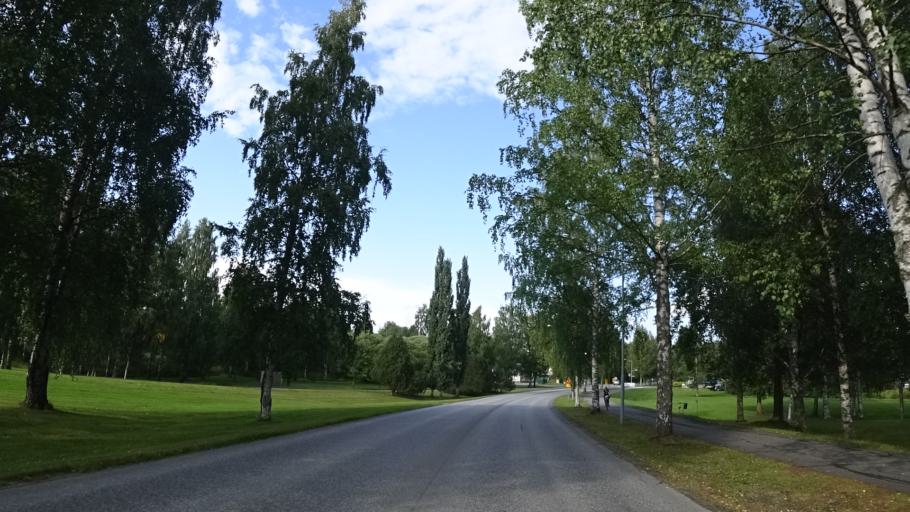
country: FI
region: North Karelia
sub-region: Pielisen Karjala
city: Lieksa
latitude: 63.3284
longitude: 30.0228
